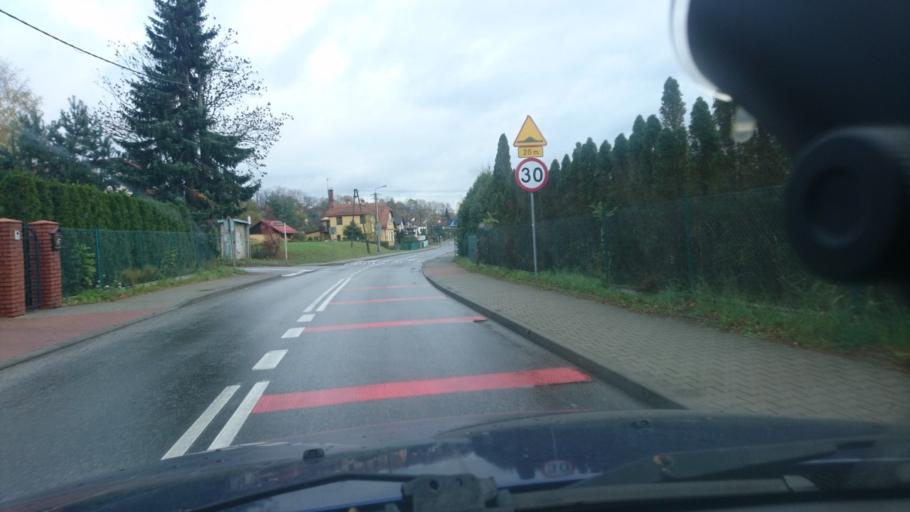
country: PL
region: Silesian Voivodeship
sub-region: Bielsko-Biala
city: Bielsko-Biala
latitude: 49.8279
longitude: 19.0212
